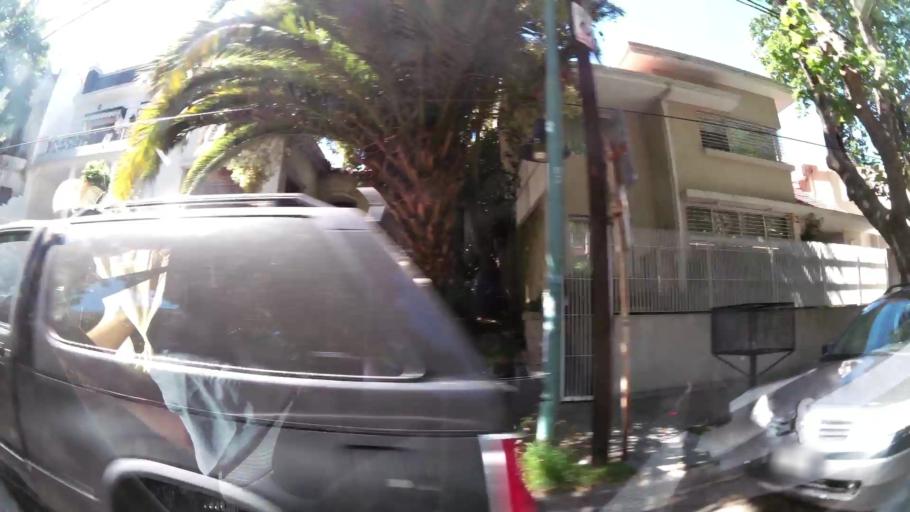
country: AR
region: Buenos Aires
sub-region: Partido de Vicente Lopez
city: Olivos
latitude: -34.5278
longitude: -58.4765
